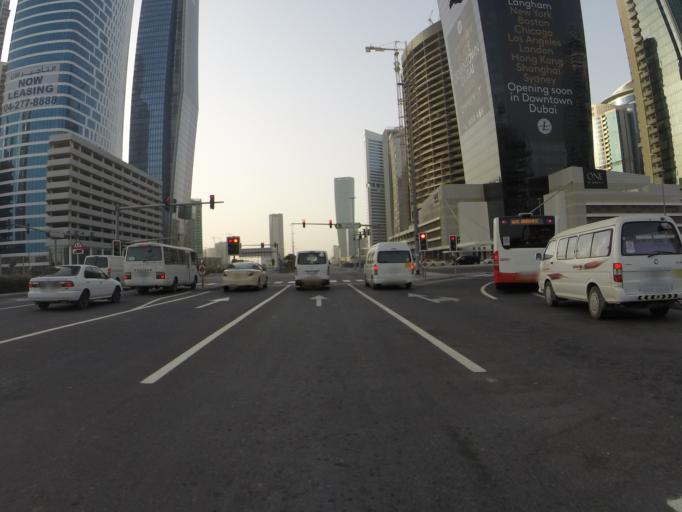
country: AE
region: Dubai
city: Dubai
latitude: 25.1892
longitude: 55.2611
